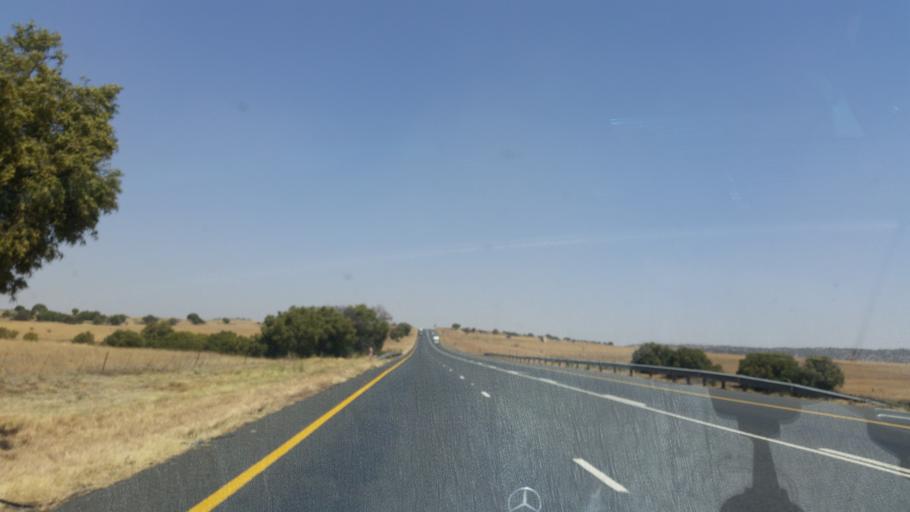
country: ZA
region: Orange Free State
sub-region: Lejweleputswa District Municipality
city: Winburg
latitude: -28.6860
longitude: 26.8217
